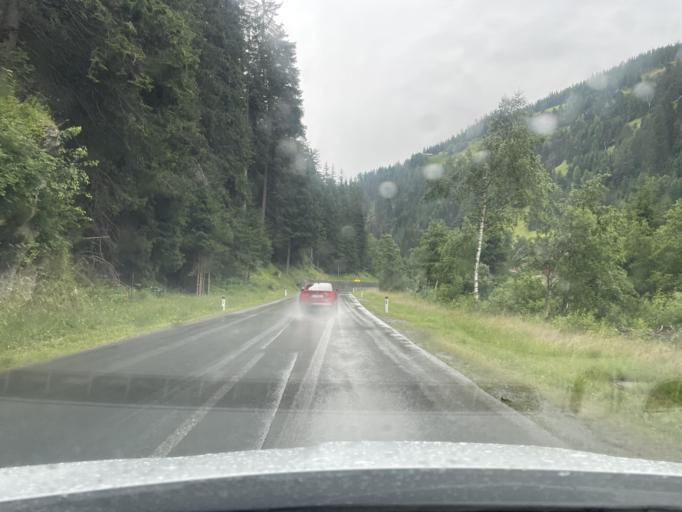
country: AT
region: Tyrol
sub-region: Politischer Bezirk Lienz
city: Sillian
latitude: 46.7684
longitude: 12.4292
